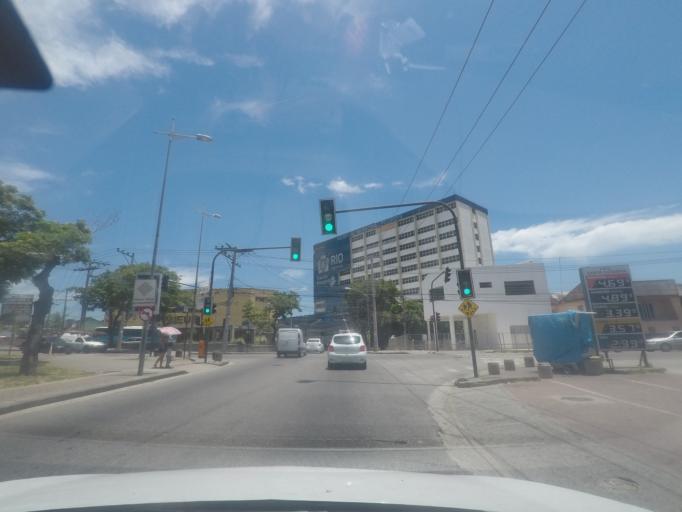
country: BR
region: Rio de Janeiro
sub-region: Itaguai
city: Itaguai
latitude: -22.9117
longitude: -43.6875
